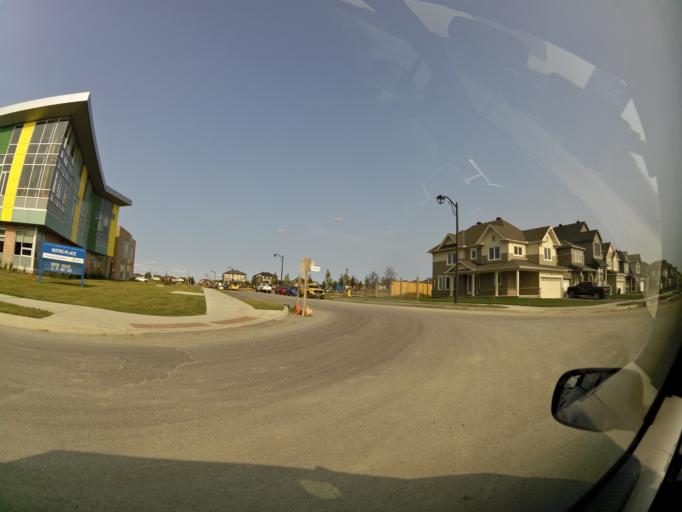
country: CA
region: Ontario
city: Ottawa
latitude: 45.4466
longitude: -75.4854
